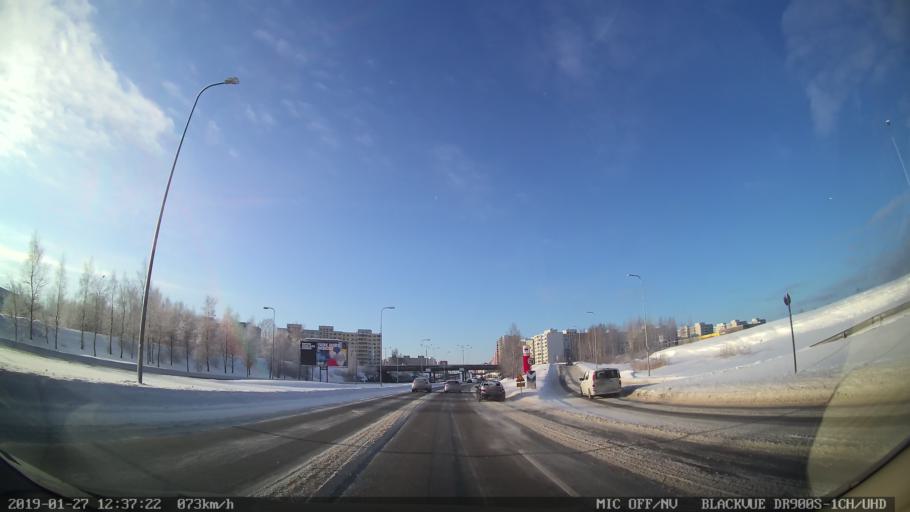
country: EE
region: Harju
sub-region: Tallinna linn
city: Kose
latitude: 59.4411
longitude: 24.8553
